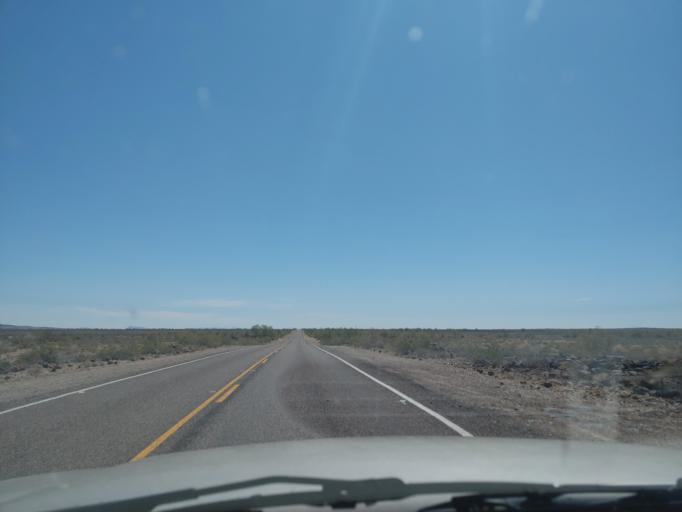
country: US
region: Arizona
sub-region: Maricopa County
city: Gila Bend
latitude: 32.9009
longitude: -113.2567
